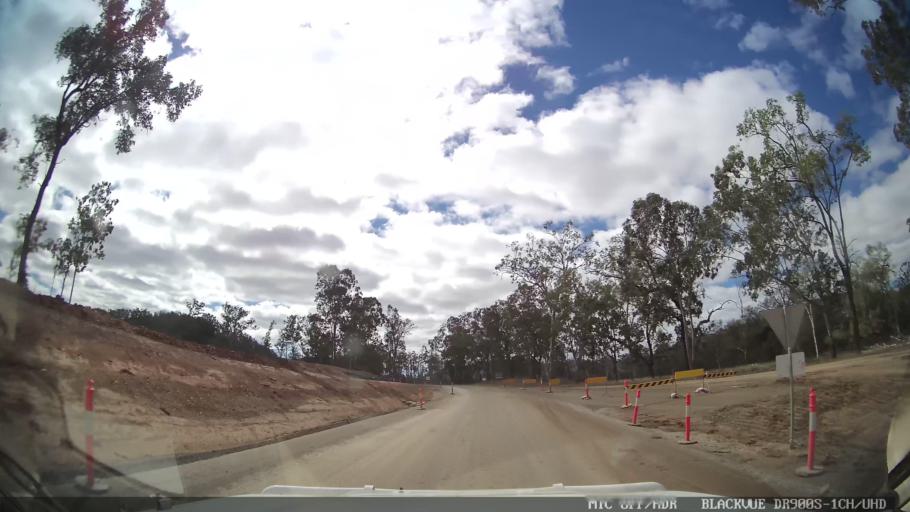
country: AU
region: Queensland
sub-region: Gladstone
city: Toolooa
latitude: -24.6137
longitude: 151.2997
